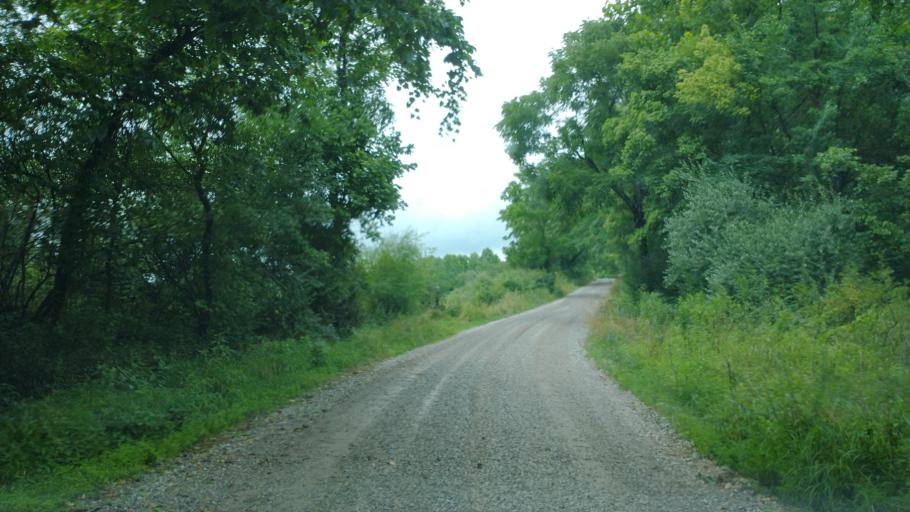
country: US
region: Ohio
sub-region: Meigs County
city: Middleport
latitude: 38.9253
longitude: -82.0547
